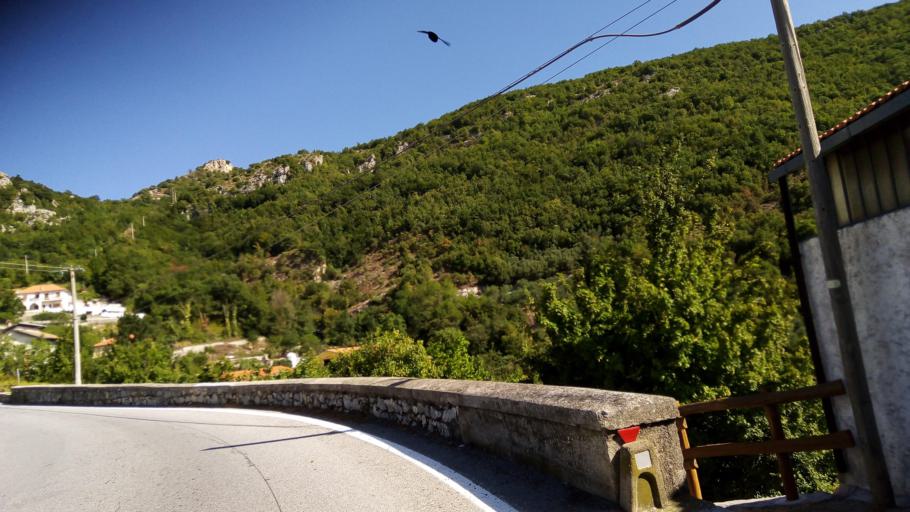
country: IT
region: Liguria
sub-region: Provincia di Savona
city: Balestrino
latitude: 44.1424
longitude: 8.1658
